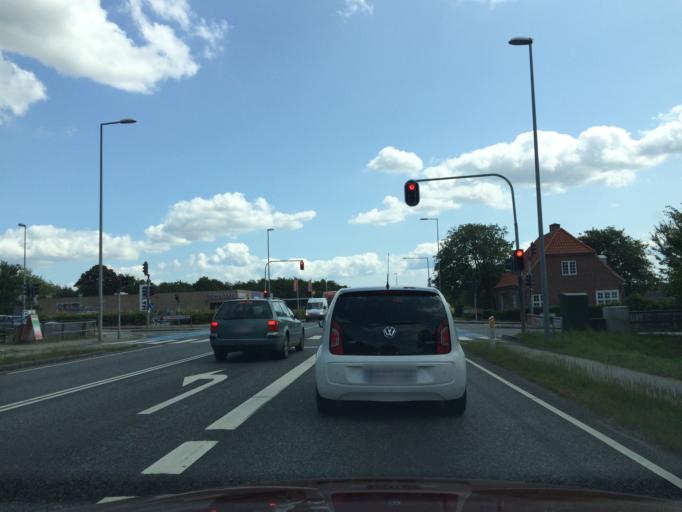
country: DK
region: Central Jutland
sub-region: Arhus Kommune
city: Sabro
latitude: 56.2111
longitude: 10.0207
